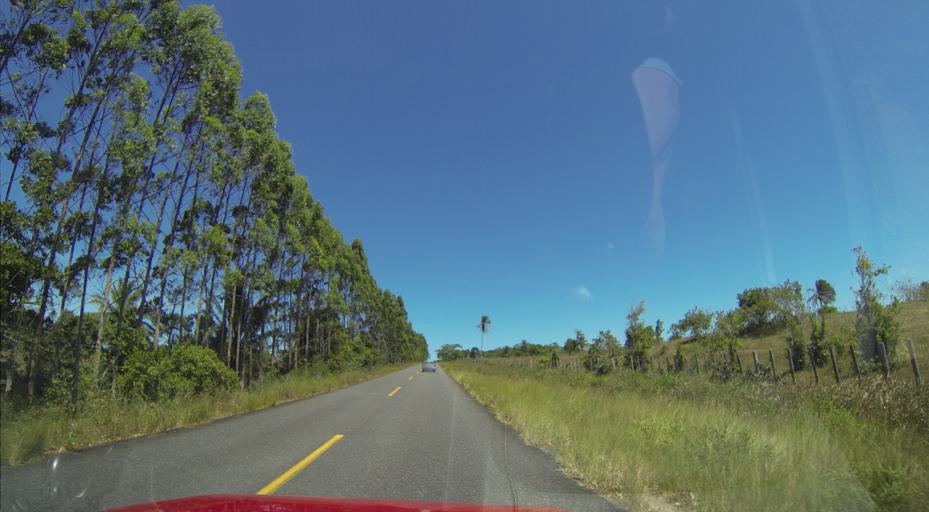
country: BR
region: Bahia
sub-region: Prado
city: Prado
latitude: -17.2672
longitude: -39.3414
